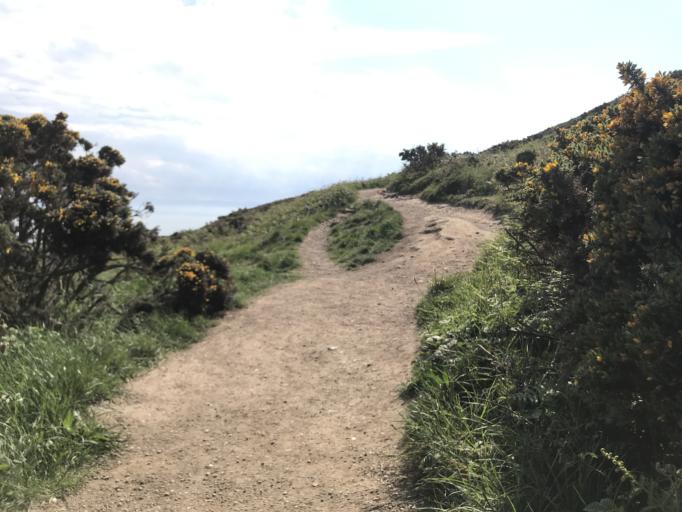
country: IE
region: Leinster
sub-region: Fingal County
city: Howth
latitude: 53.3710
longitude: -6.0512
